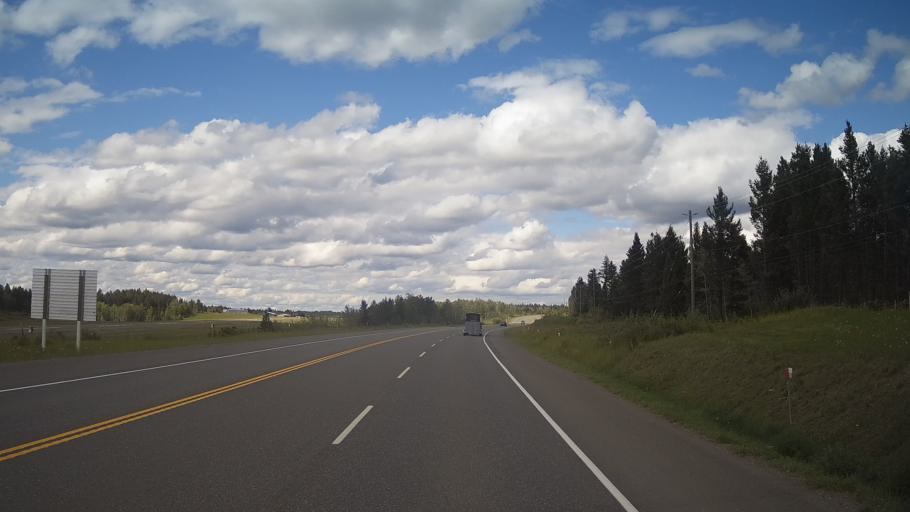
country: CA
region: British Columbia
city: Williams Lake
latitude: 51.7338
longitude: -121.3304
